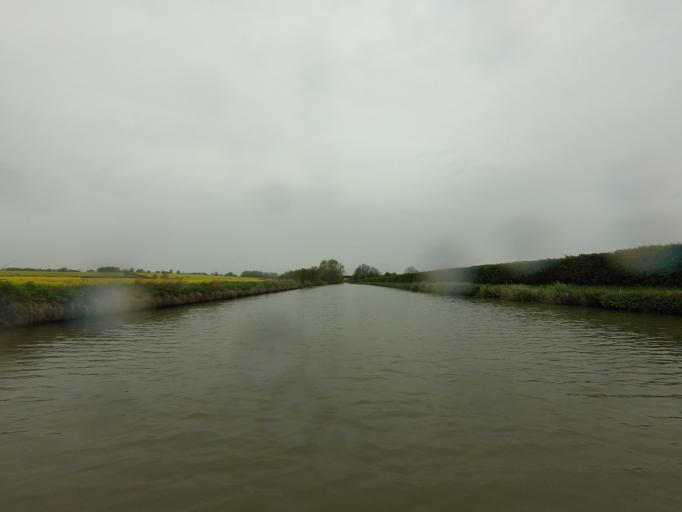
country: GB
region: England
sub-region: Northamptonshire
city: Hartwell
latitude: 52.1074
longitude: -0.8867
